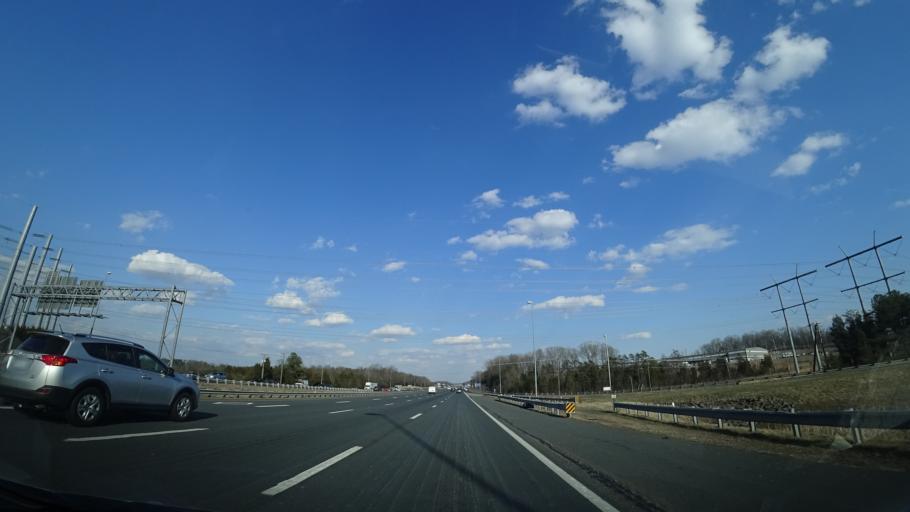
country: US
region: Virginia
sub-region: Prince William County
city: Linton Hall
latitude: 38.7981
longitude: -77.5660
